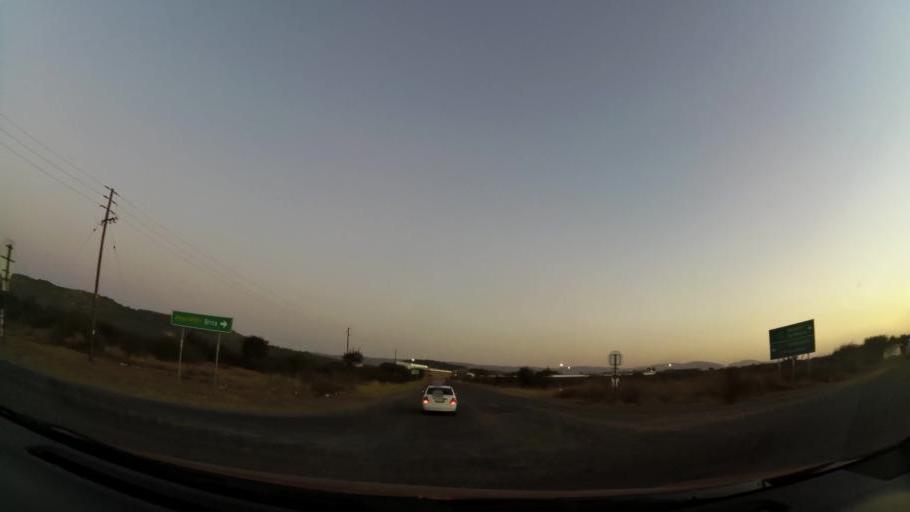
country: ZA
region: North-West
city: Ga-Rankuwa
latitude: -25.6237
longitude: 27.9627
